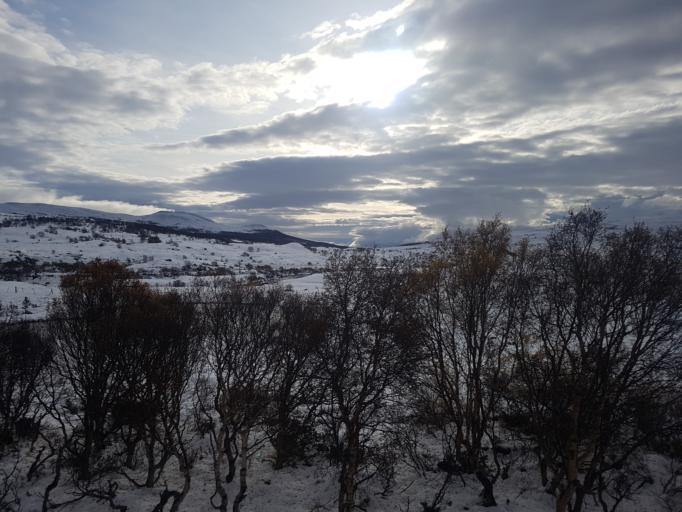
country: NO
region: Sor-Trondelag
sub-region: Oppdal
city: Oppdal
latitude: 62.2757
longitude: 9.5839
